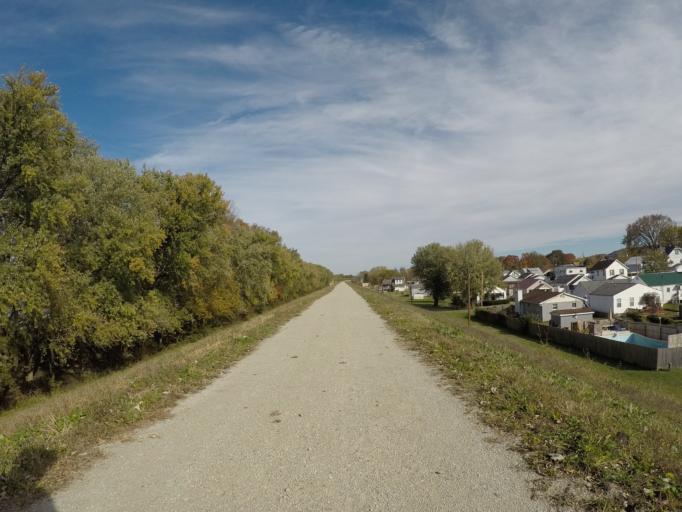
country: US
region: Ohio
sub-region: Lawrence County
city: Burlington
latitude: 38.4104
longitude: -82.4953
